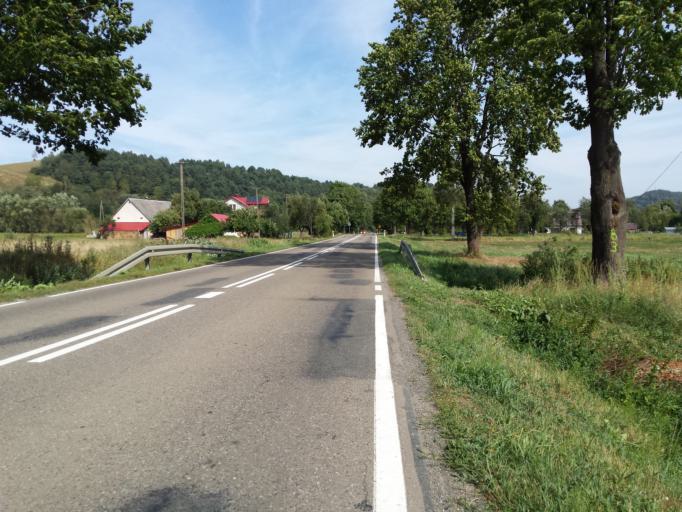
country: PL
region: Subcarpathian Voivodeship
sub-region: Powiat leski
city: Baligrod
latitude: 49.3747
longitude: 22.2757
